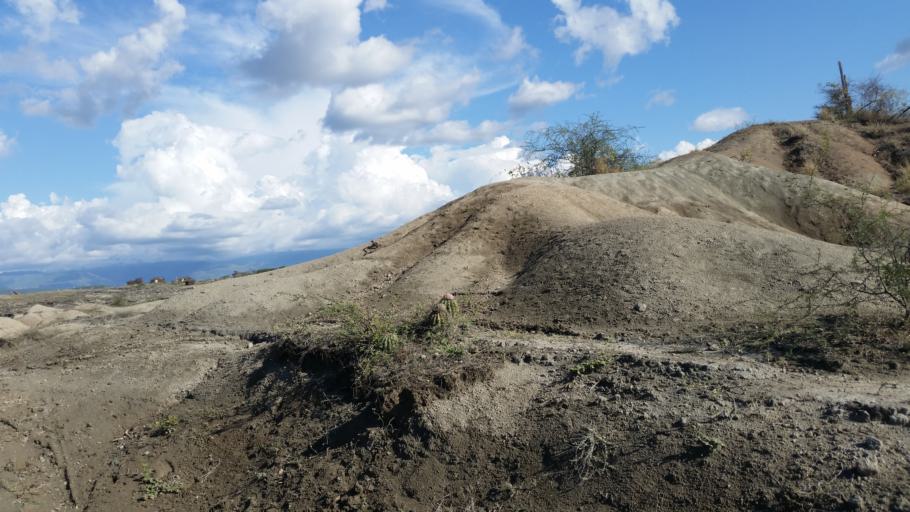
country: CO
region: Huila
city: Villavieja
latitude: 3.2542
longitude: -75.1335
